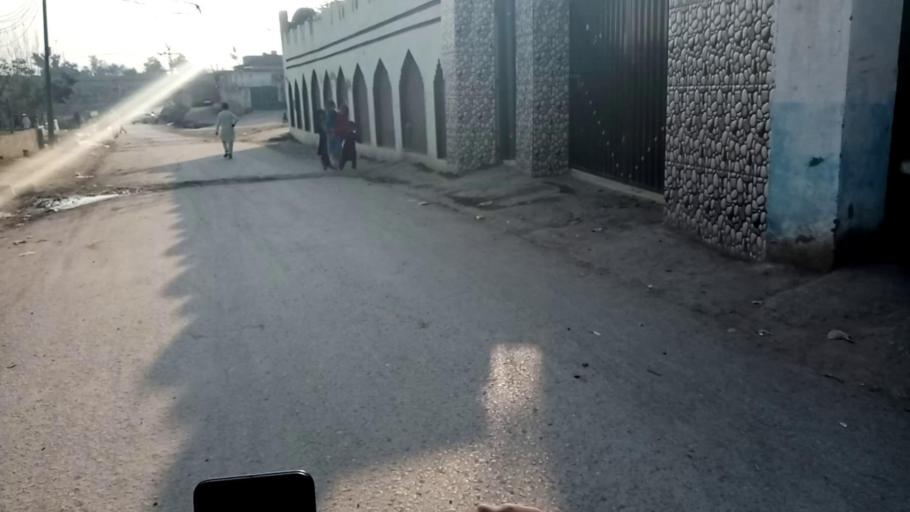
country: PK
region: Khyber Pakhtunkhwa
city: Peshawar
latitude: 34.0060
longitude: 71.4679
